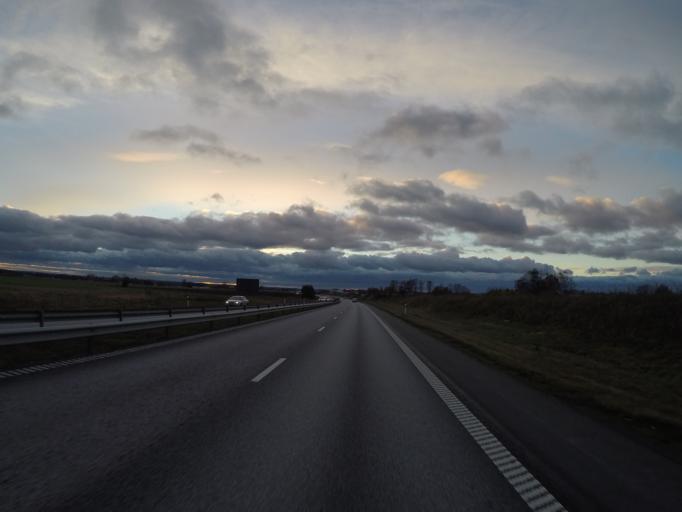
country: SE
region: Skane
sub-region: Kristianstads Kommun
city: Fjalkinge
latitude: 56.0305
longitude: 14.2307
